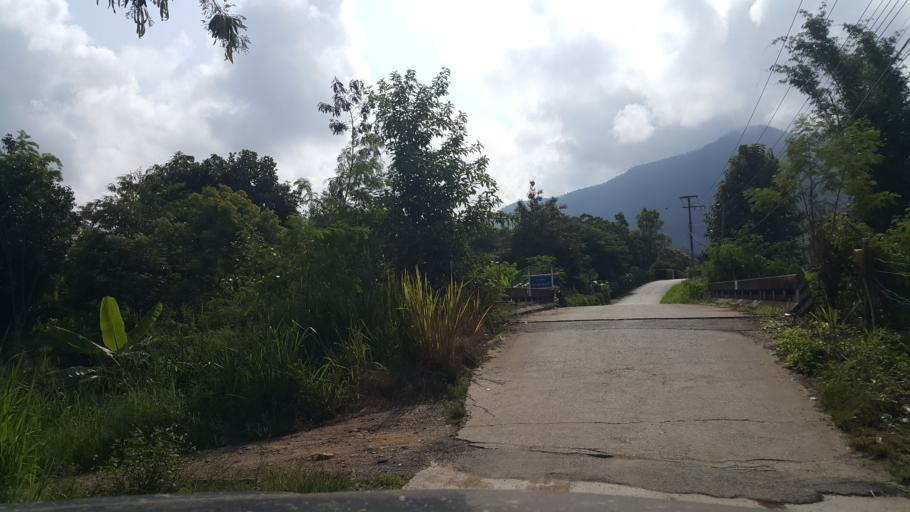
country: TH
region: Chiang Mai
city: Mae On
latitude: 18.7415
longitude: 99.2299
